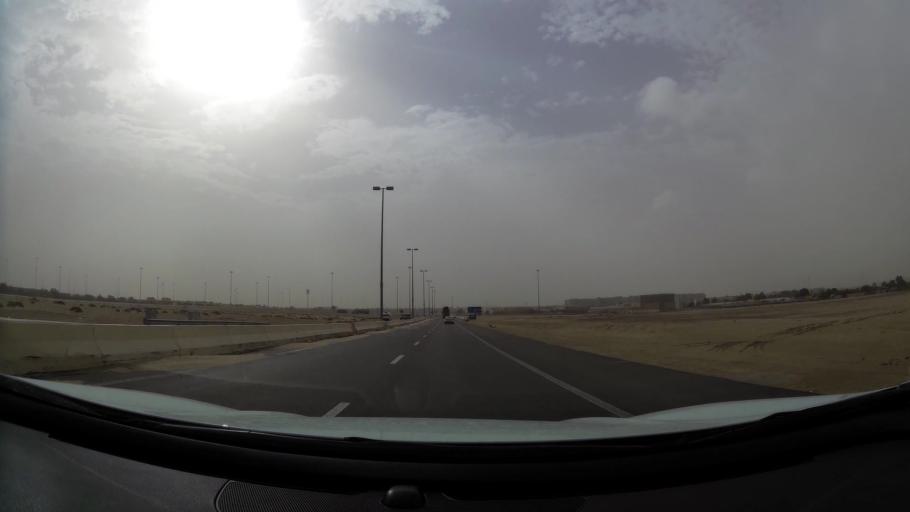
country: AE
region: Abu Dhabi
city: Abu Dhabi
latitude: 24.4666
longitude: 54.6730
